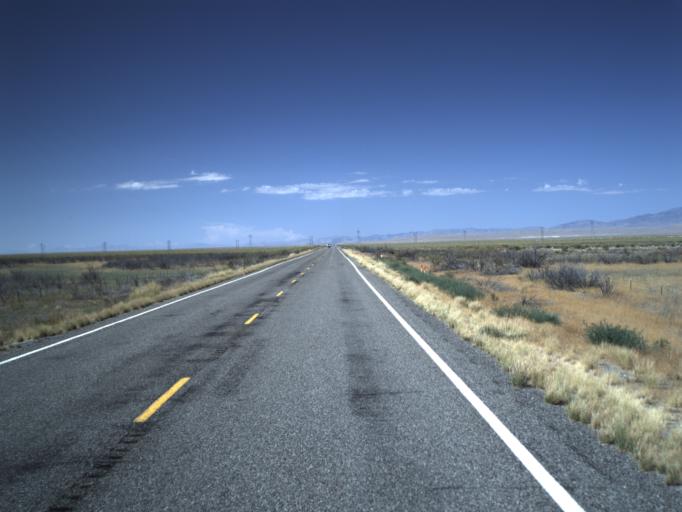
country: US
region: Utah
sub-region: Millard County
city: Delta
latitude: 39.2607
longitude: -112.8796
